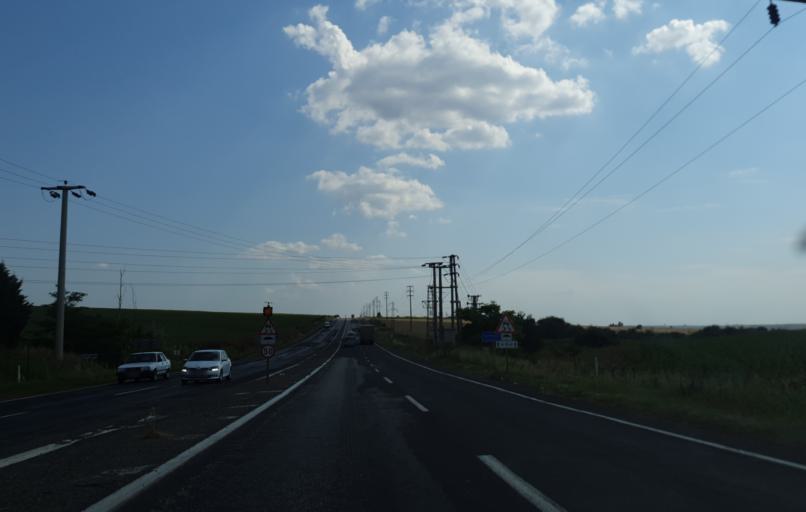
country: TR
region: Kirklareli
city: Buyukkaristiran
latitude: 41.2619
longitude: 27.5477
